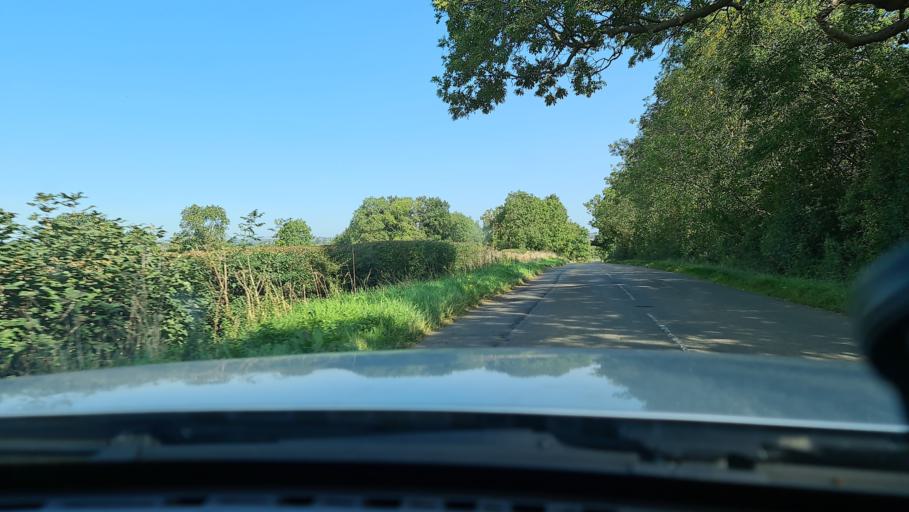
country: GB
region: England
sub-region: Northamptonshire
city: Brackley
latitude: 52.1199
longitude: -1.1905
